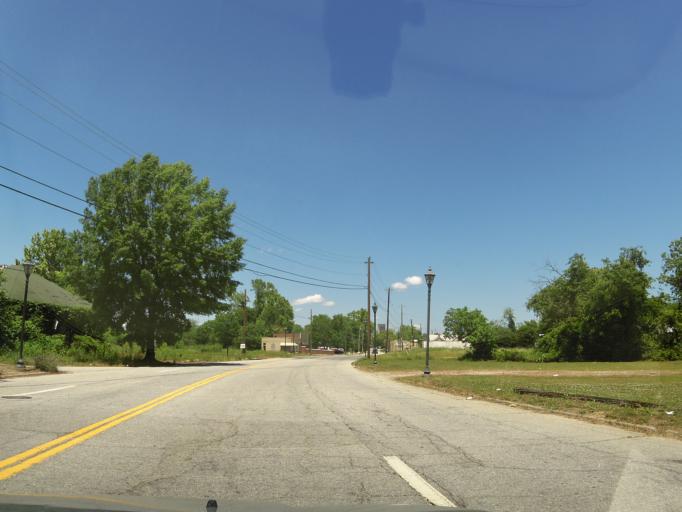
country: US
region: Georgia
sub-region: Richmond County
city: Augusta
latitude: 33.4634
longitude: -81.9690
